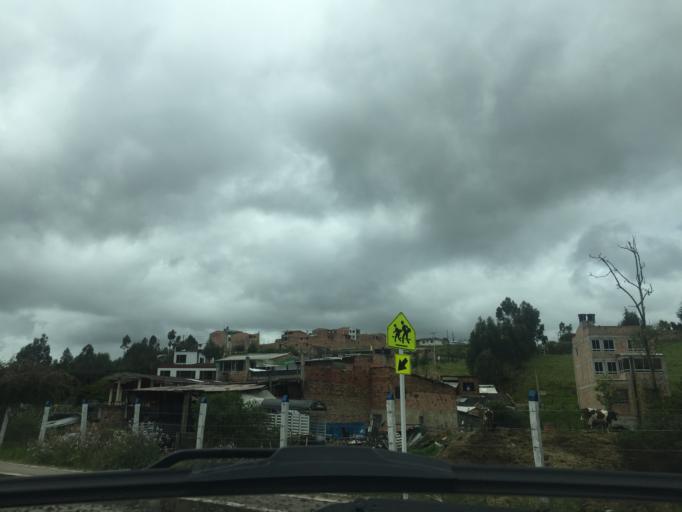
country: CO
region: Cundinamarca
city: Villapinzon
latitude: 5.2201
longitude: -73.5938
